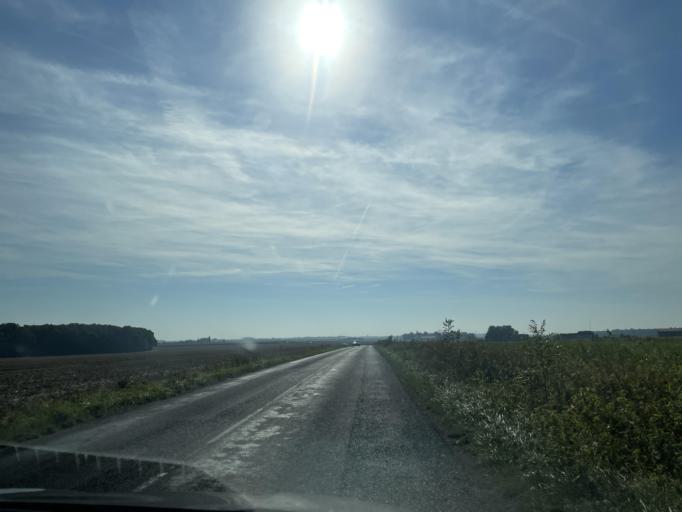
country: FR
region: Ile-de-France
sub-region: Departement de Seine-et-Marne
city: Sammeron
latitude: 48.8897
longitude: 3.0667
